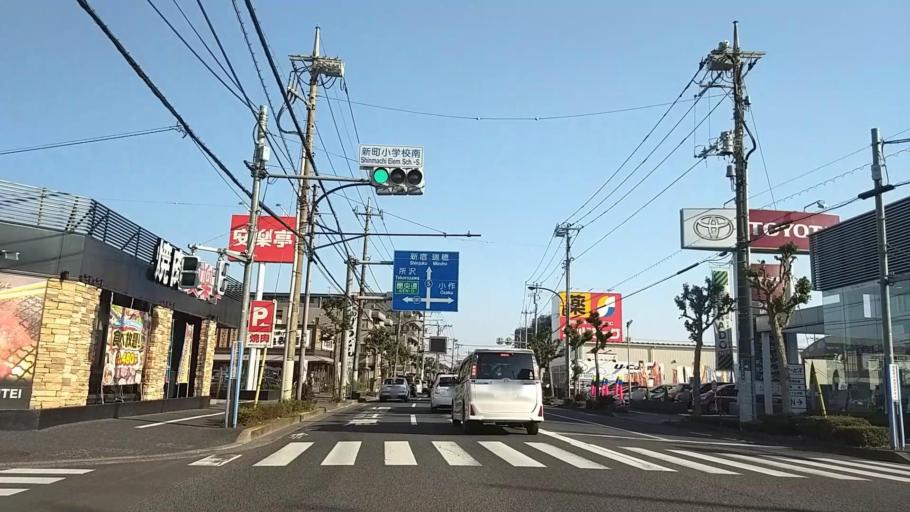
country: JP
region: Tokyo
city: Fussa
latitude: 35.7861
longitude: 139.3083
